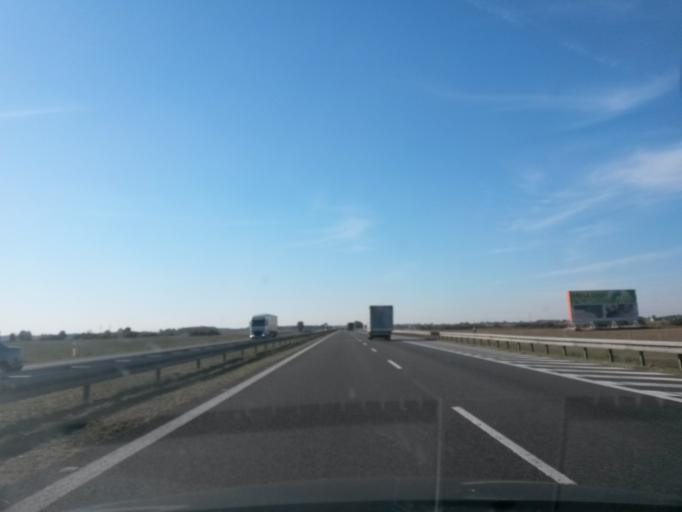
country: PL
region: Opole Voivodeship
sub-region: Powiat brzeski
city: Lewin Brzeski
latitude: 50.7122
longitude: 17.5850
